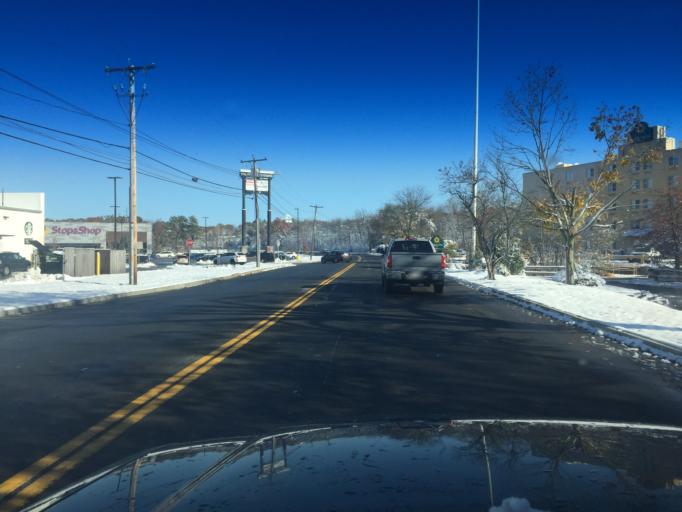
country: US
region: Massachusetts
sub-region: Worcester County
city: Milford
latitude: 42.1484
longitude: -71.4873
